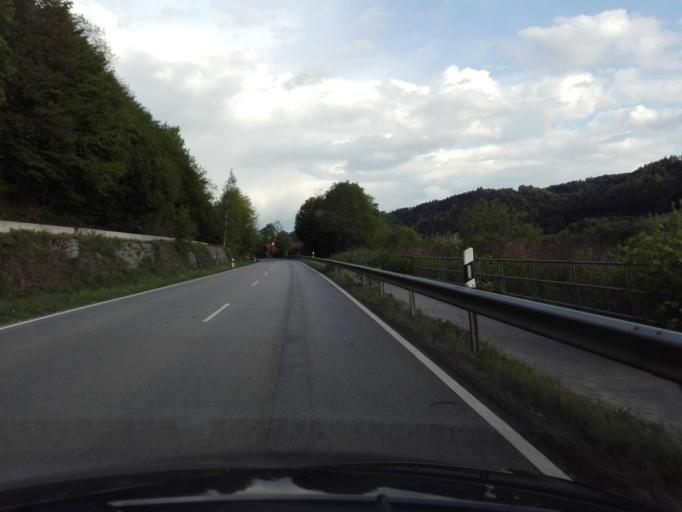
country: DE
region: Bavaria
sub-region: Lower Bavaria
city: Obernzell
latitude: 48.5632
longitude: 13.6135
